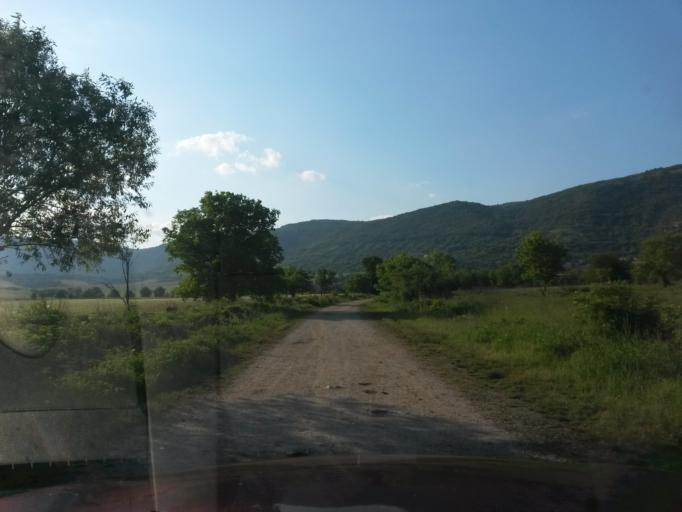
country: SK
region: Kosicky
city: Roznava
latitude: 48.5859
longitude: 20.6756
